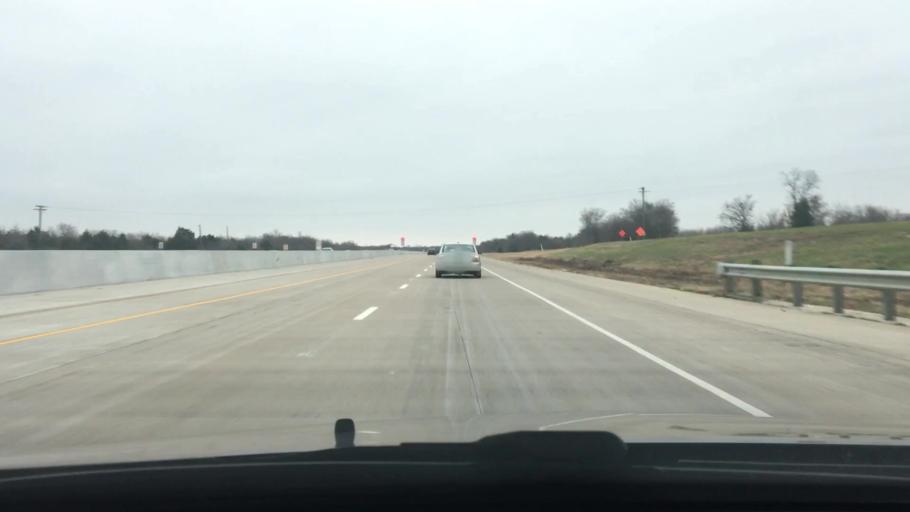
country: US
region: Texas
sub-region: Freestone County
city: Wortham
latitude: 31.8787
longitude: -96.3445
